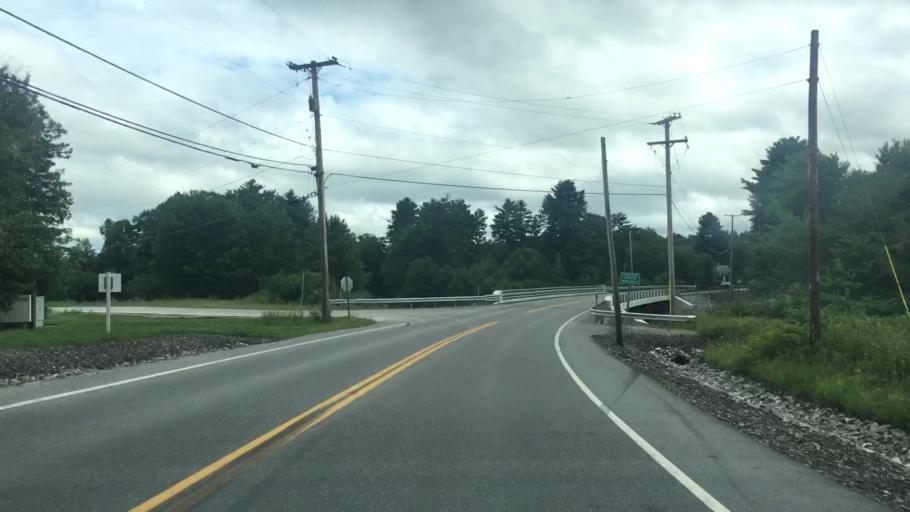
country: US
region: Maine
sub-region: York County
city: Lake Arrowhead
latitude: 43.6536
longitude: -70.7608
